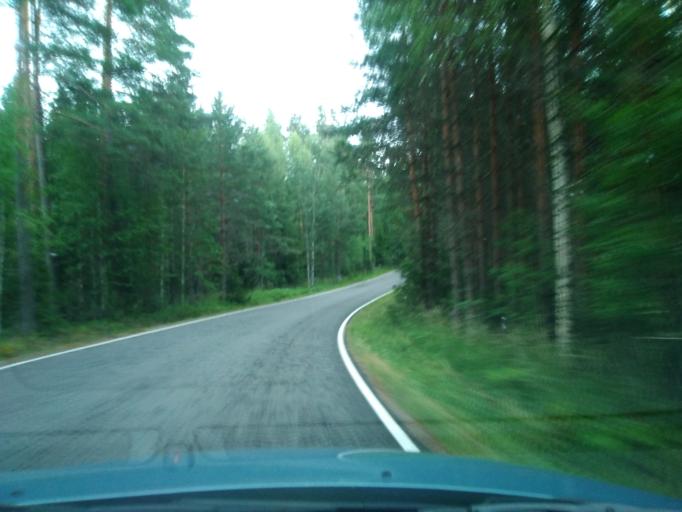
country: FI
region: Uusimaa
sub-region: Helsinki
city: Kaerkoelae
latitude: 60.7863
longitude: 24.0806
